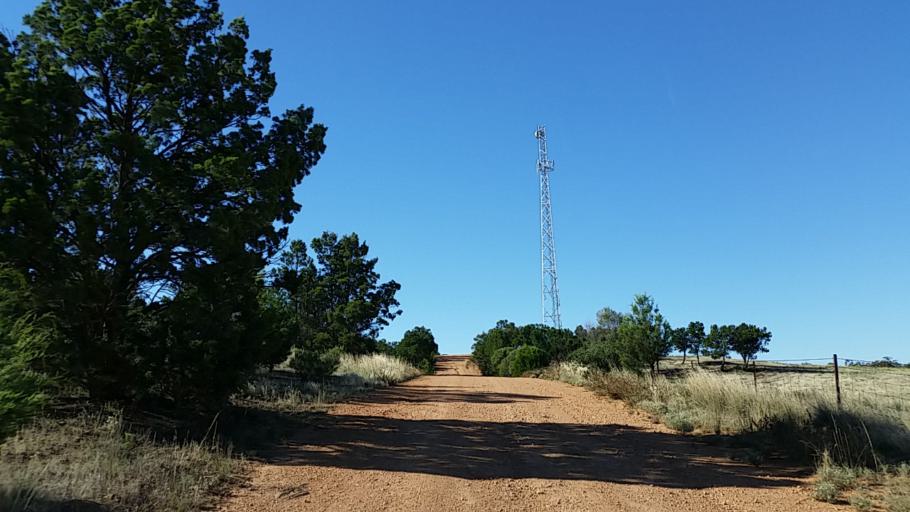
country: AU
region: South Australia
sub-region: Peterborough
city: Peterborough
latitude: -32.9604
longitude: 138.8317
